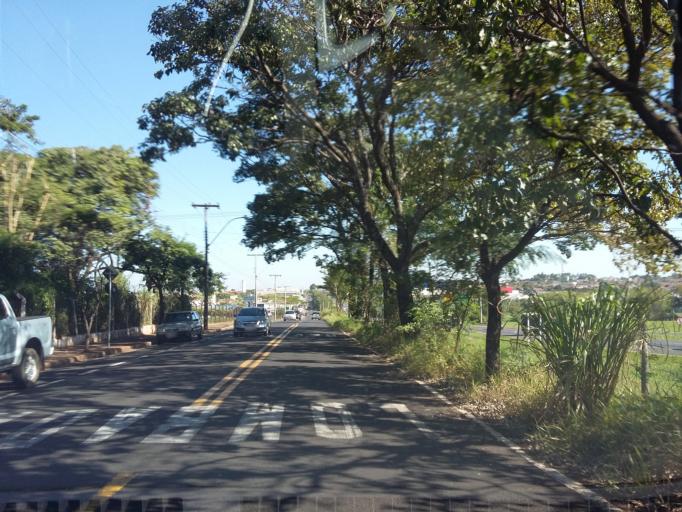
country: BR
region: Sao Paulo
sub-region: Sao Jose Do Rio Preto
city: Sao Jose do Rio Preto
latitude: -20.8342
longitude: -49.3641
